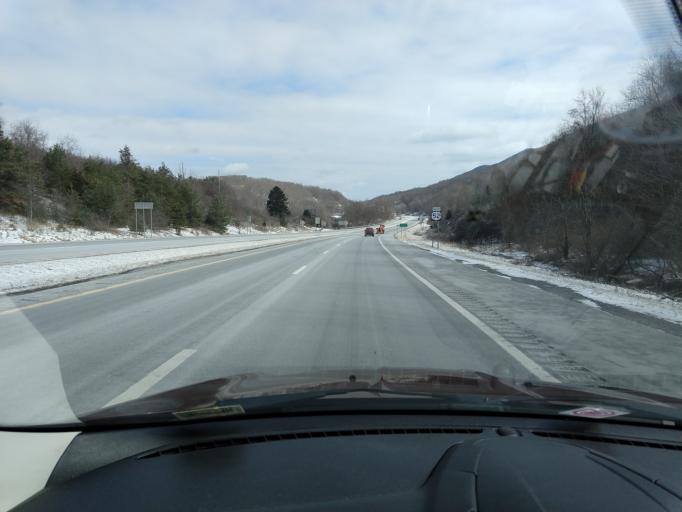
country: US
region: West Virginia
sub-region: Mercer County
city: Bluefield
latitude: 37.2750
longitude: -81.1519
